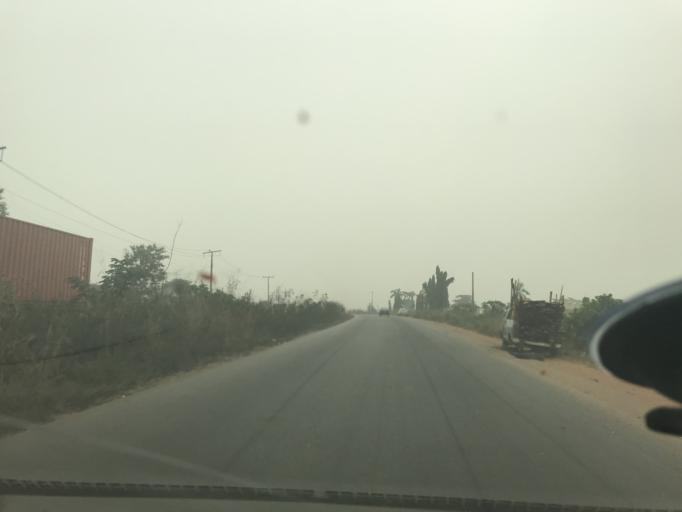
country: NG
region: Ogun
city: Shagamu
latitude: 6.8628
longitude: 3.6221
